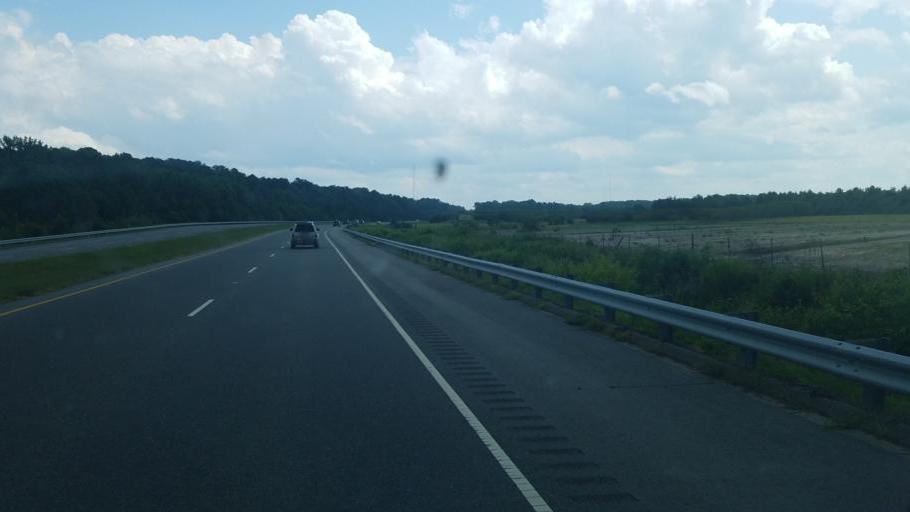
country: US
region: North Carolina
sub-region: Currituck County
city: Moyock
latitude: 36.6464
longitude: -76.2221
